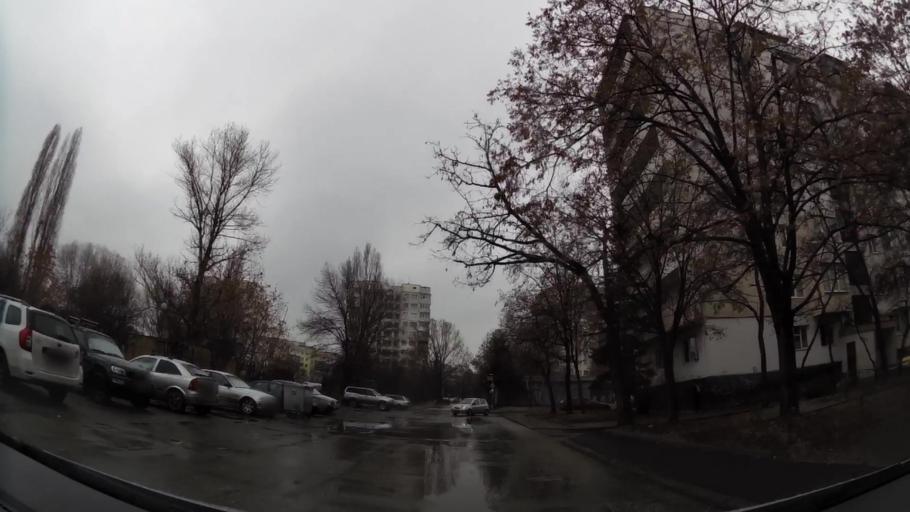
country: BG
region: Sofia-Capital
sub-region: Stolichna Obshtina
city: Sofia
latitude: 42.6698
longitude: 23.3912
